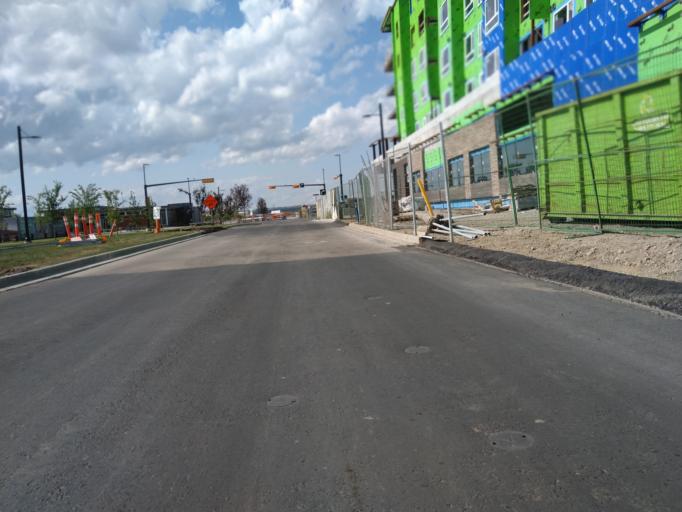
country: CA
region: Alberta
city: Calgary
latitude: 51.0768
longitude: -114.1470
